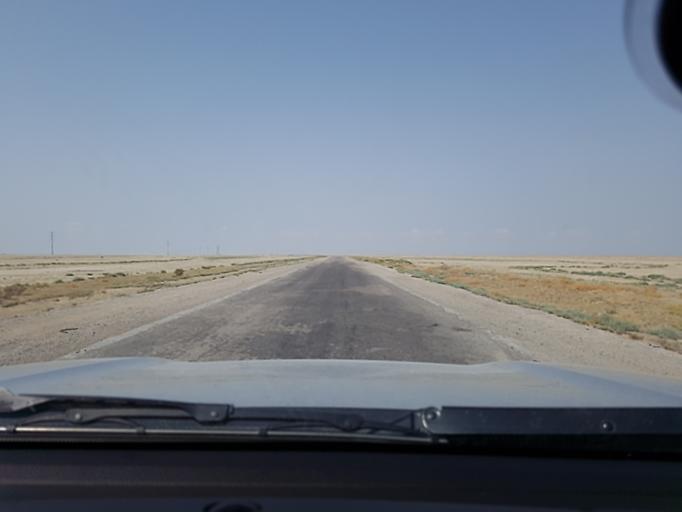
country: TM
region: Balkan
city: Gumdag
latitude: 38.7188
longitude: 54.4707
